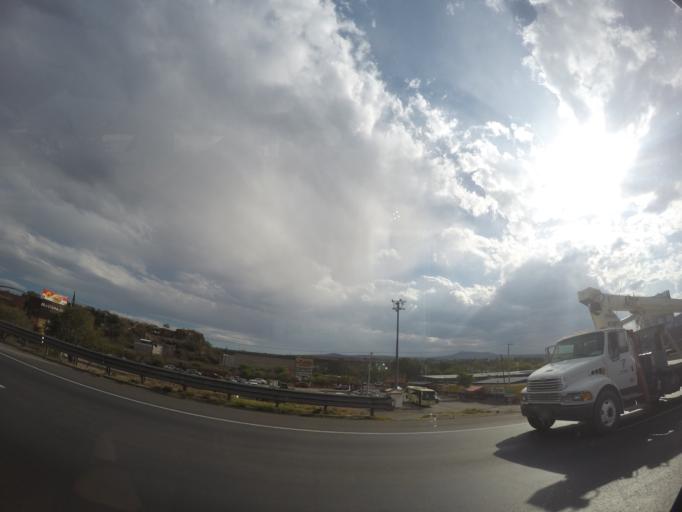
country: MX
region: Mexico
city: San Francisco Soyaniquilpan
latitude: 20.0089
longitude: -99.5070
